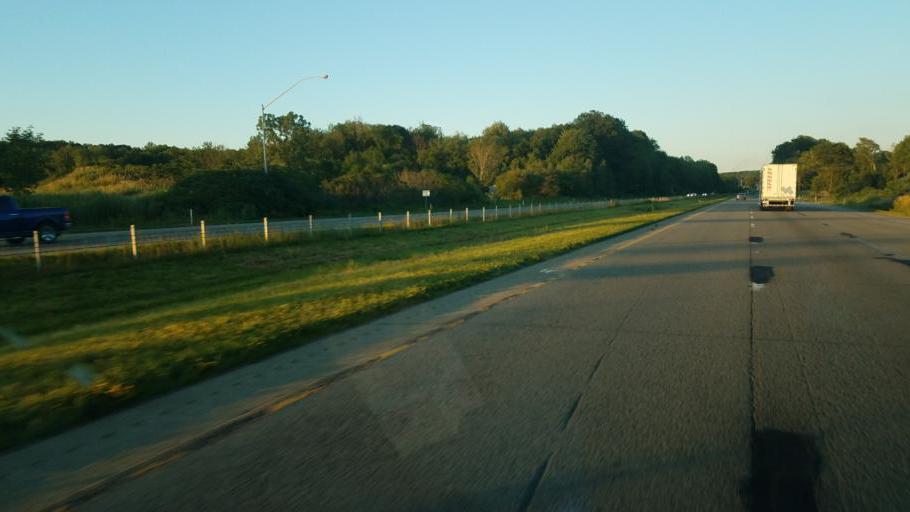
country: US
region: Pennsylvania
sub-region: Erie County
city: Fairview
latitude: 42.0191
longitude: -80.1838
